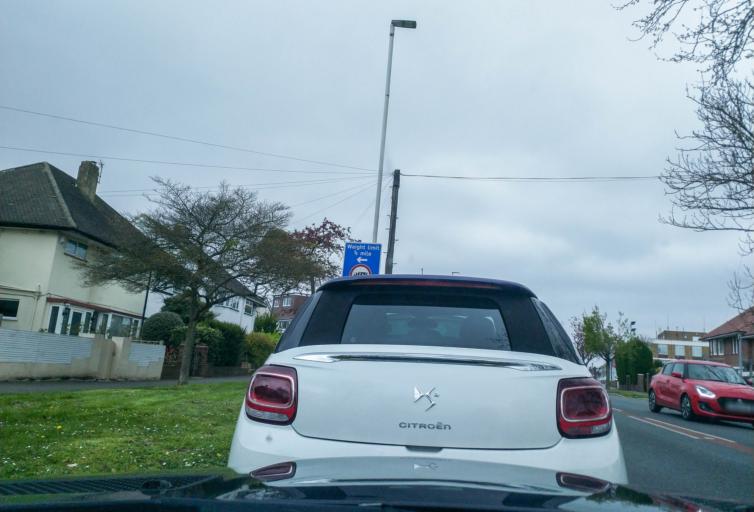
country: GB
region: England
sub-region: Greater London
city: Pinner
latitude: 51.5735
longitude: -0.3951
